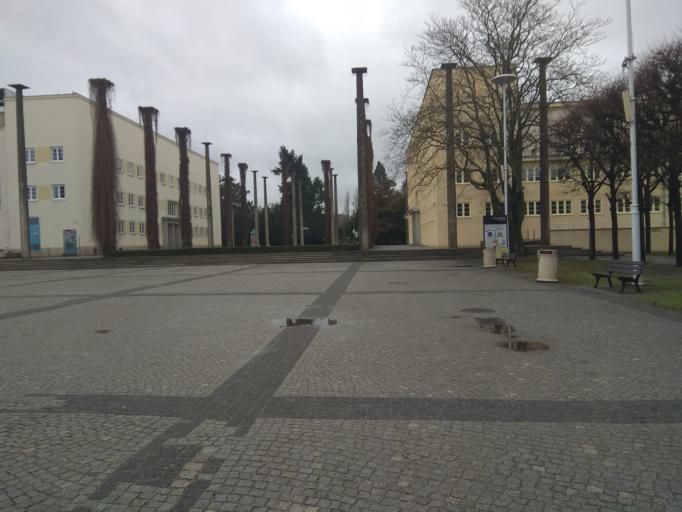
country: PL
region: Lower Silesian Voivodeship
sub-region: Powiat wroclawski
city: Wroclaw
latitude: 51.1077
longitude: 17.0754
